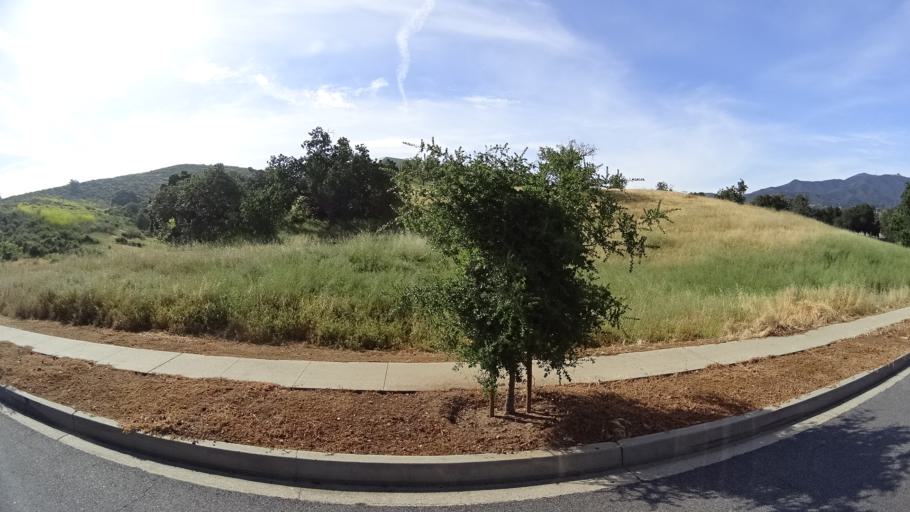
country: US
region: California
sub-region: Ventura County
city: Thousand Oaks
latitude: 34.1883
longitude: -118.8856
